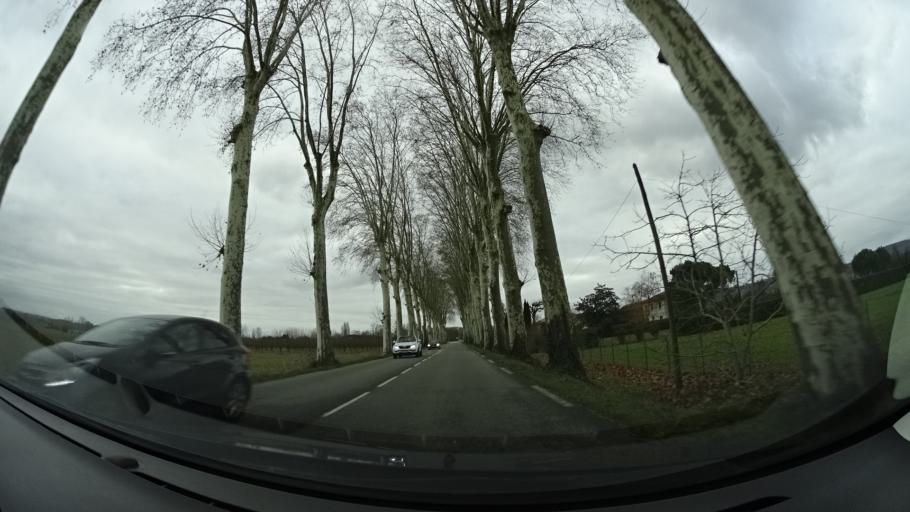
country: FR
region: Aquitaine
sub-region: Departement du Lot-et-Garonne
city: Castelmoron-sur-Lot
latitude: 44.3766
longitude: 0.4889
